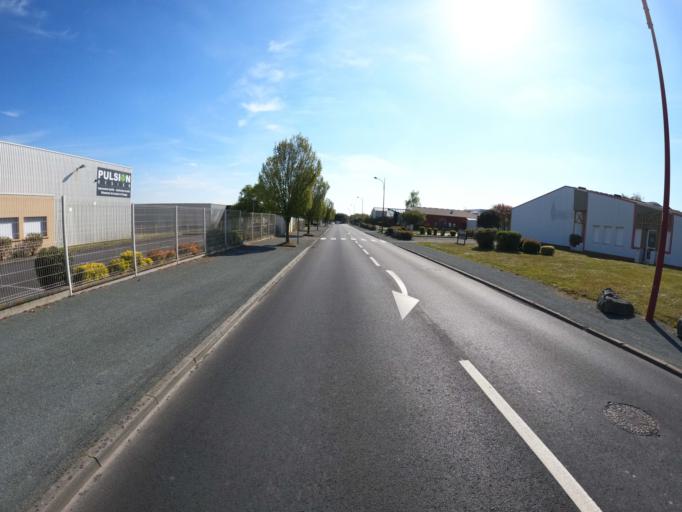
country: FR
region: Pays de la Loire
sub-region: Departement de Maine-et-Loire
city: La Seguiniere
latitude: 47.0736
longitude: -0.9344
